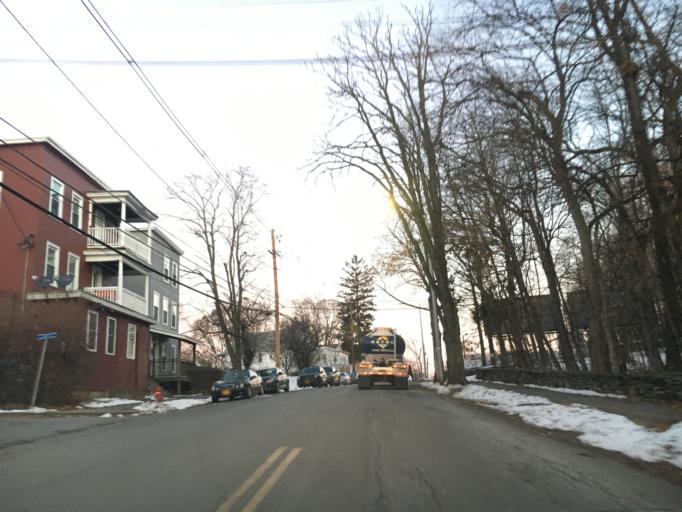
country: US
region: New York
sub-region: Dutchess County
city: Poughkeepsie
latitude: 41.6917
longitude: -73.9318
